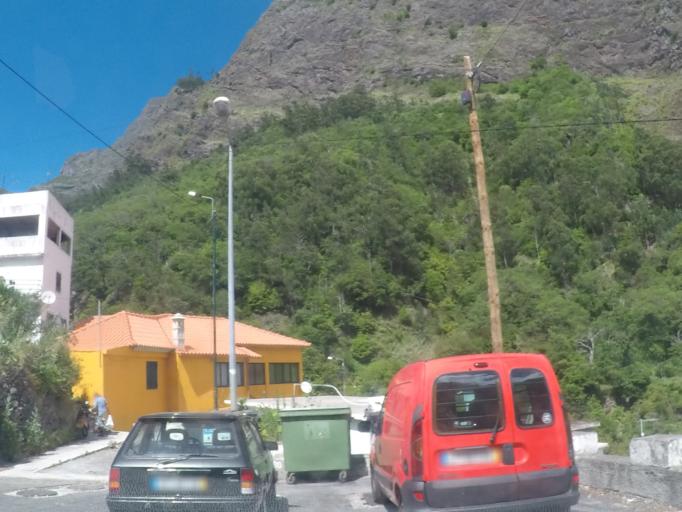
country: PT
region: Madeira
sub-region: Camara de Lobos
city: Curral das Freiras
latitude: 32.7071
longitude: -16.9716
